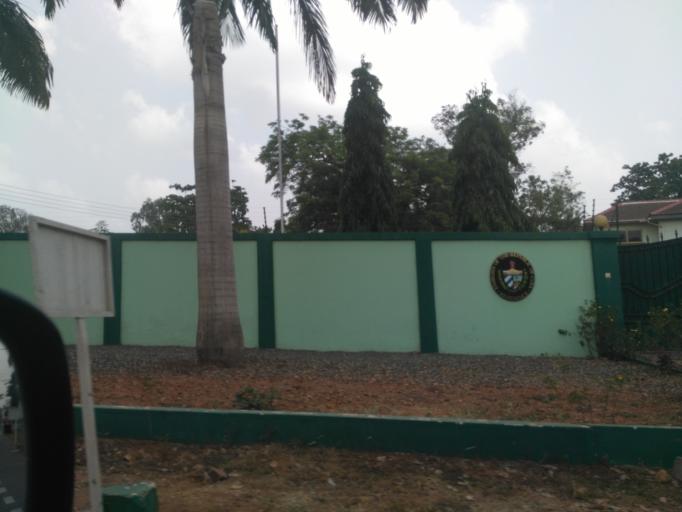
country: GH
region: Greater Accra
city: Accra
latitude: 5.6052
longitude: -0.1837
